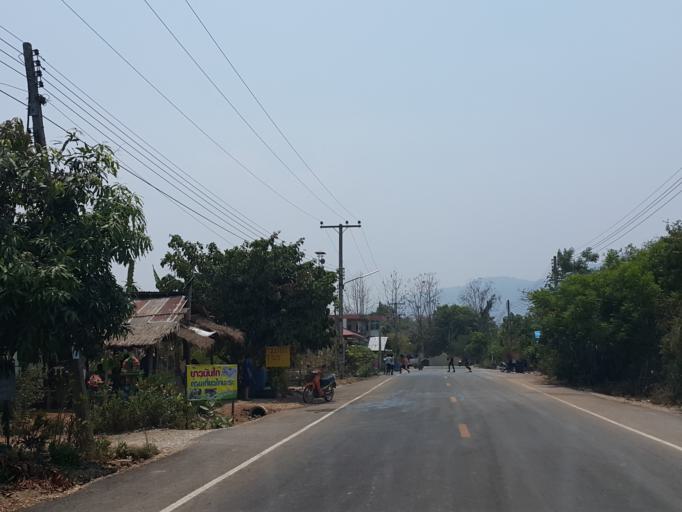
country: TH
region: Kamphaeng Phet
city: Pang Sila Thong
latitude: 15.9970
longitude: 99.3711
